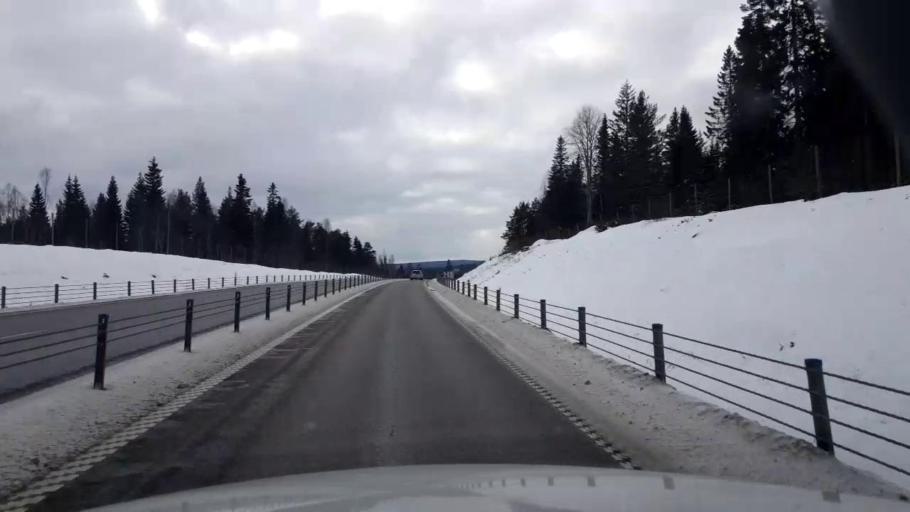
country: SE
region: Vaesternorrland
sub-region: Sundsvalls Kommun
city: Njurundabommen
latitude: 62.0918
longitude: 17.3032
